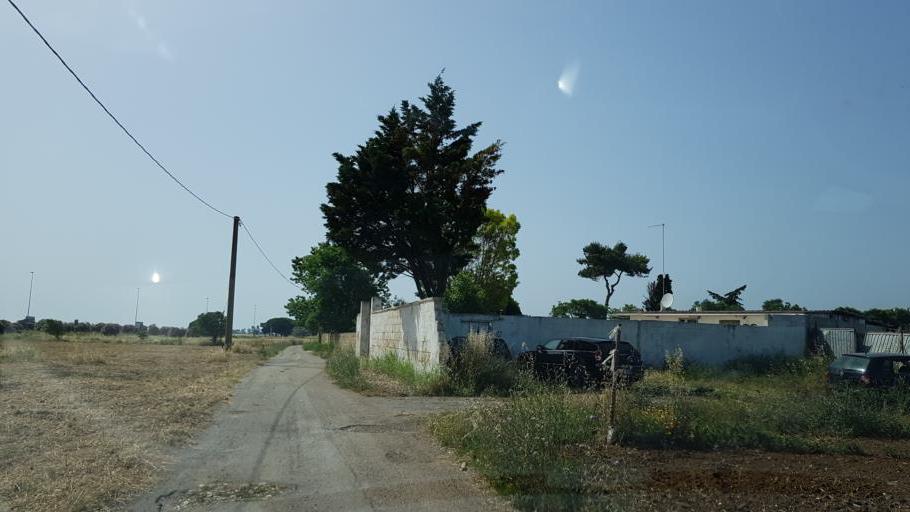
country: IT
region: Apulia
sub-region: Provincia di Brindisi
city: Brindisi
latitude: 40.6629
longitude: 17.9245
